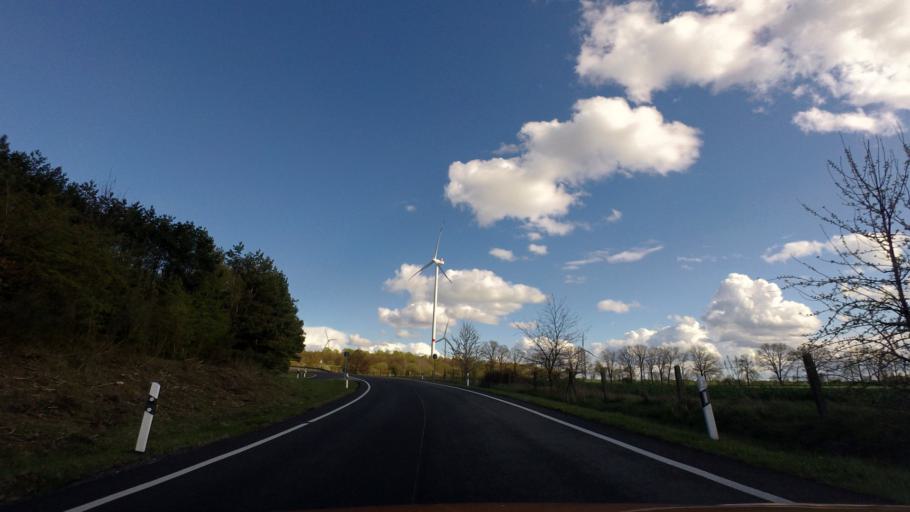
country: DE
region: Brandenburg
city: Gerdshagen
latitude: 53.2327
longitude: 12.2008
